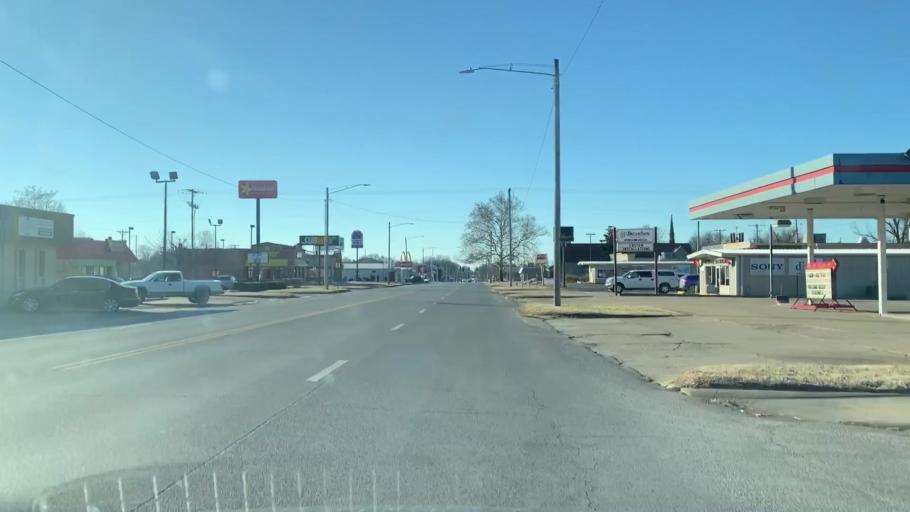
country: US
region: Kansas
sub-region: Crawford County
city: Pittsburg
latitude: 37.3993
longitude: -94.7050
